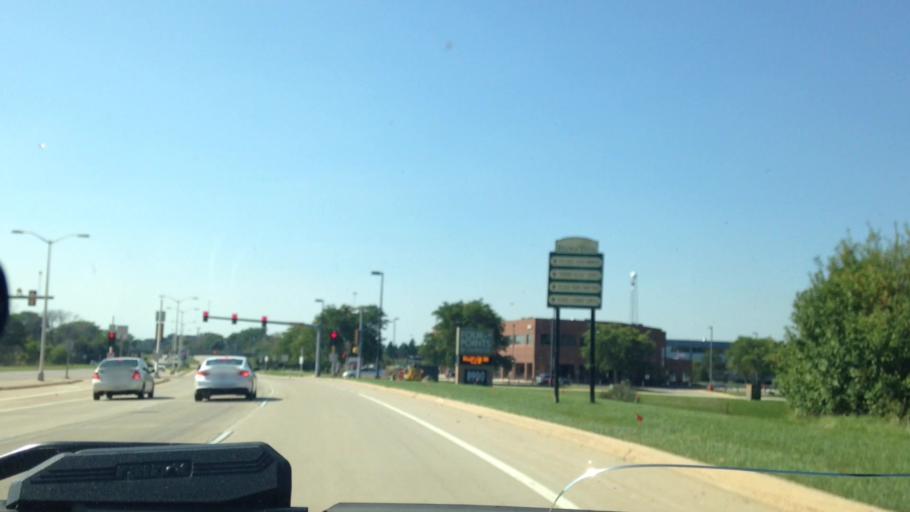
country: US
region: Wisconsin
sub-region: Milwaukee County
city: Brown Deer
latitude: 43.1785
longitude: -87.9572
